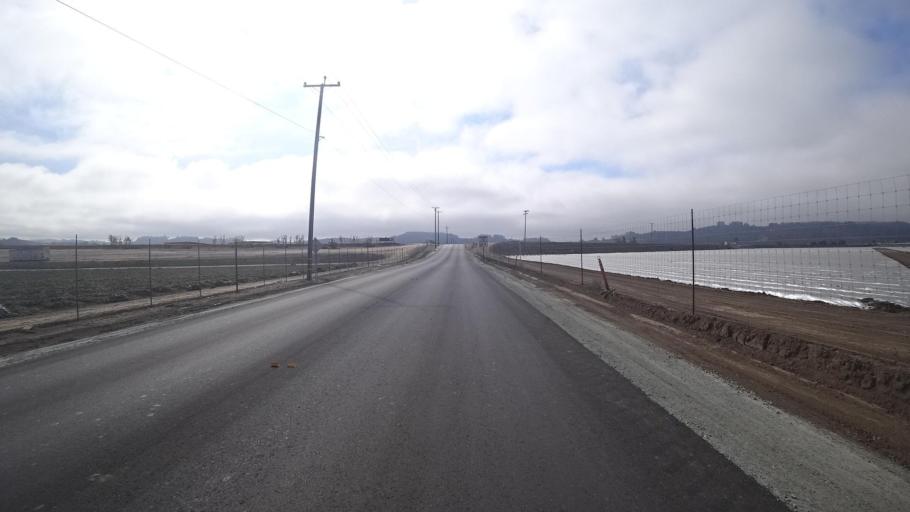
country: US
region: California
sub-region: San Benito County
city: Aromas
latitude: 36.9021
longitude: -121.6780
